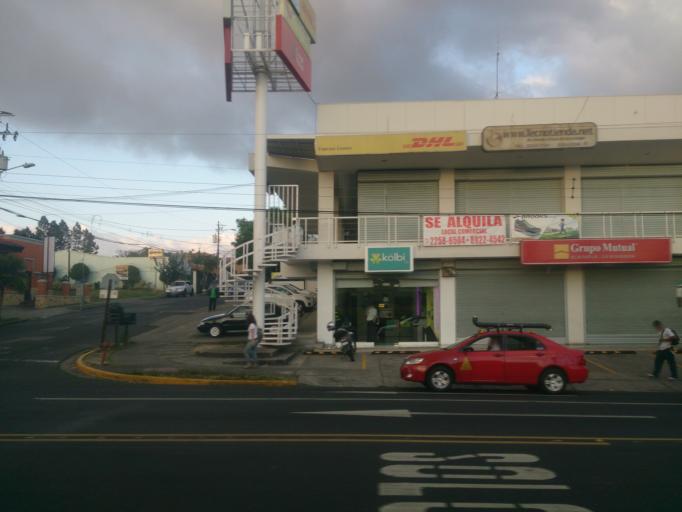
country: CR
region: San Jose
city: San Pedro
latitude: 9.9275
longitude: -84.0413
